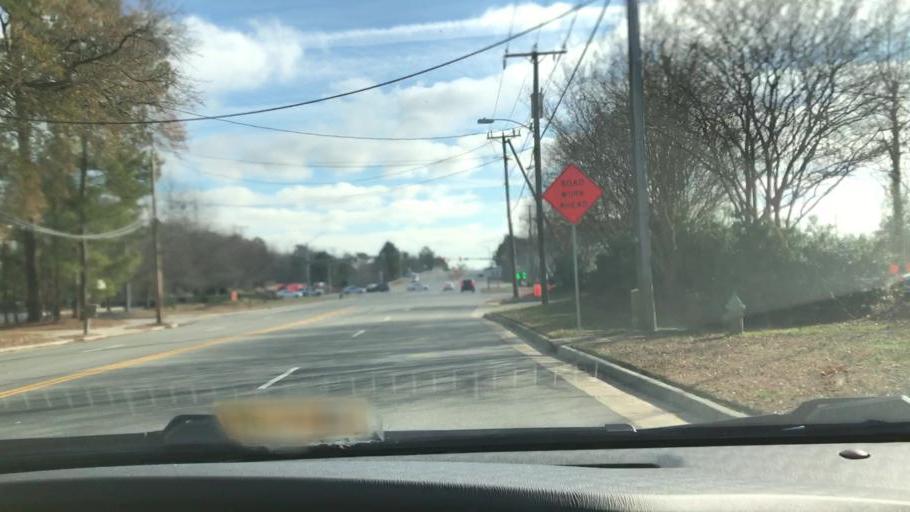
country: US
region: Virginia
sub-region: City of Chesapeake
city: Chesapeake
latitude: 36.6894
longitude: -76.2326
